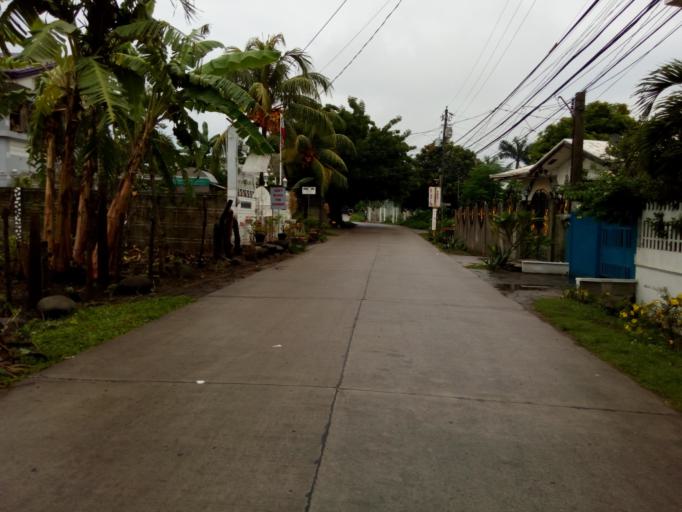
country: PH
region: Central Visayas
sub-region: Province of Negros Oriental
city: Dumaguete
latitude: 9.3212
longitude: 123.2951
